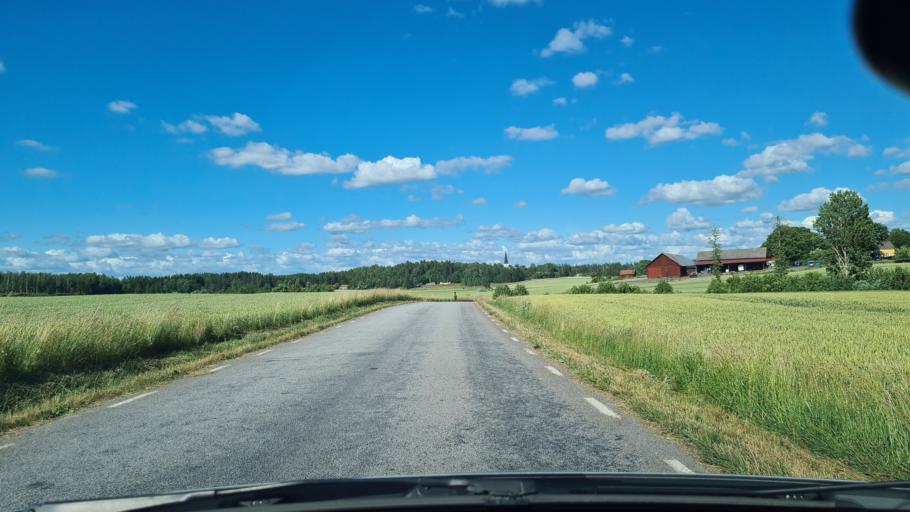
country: SE
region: Soedermanland
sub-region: Nykopings Kommun
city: Olstorp
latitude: 58.8262
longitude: 16.5073
